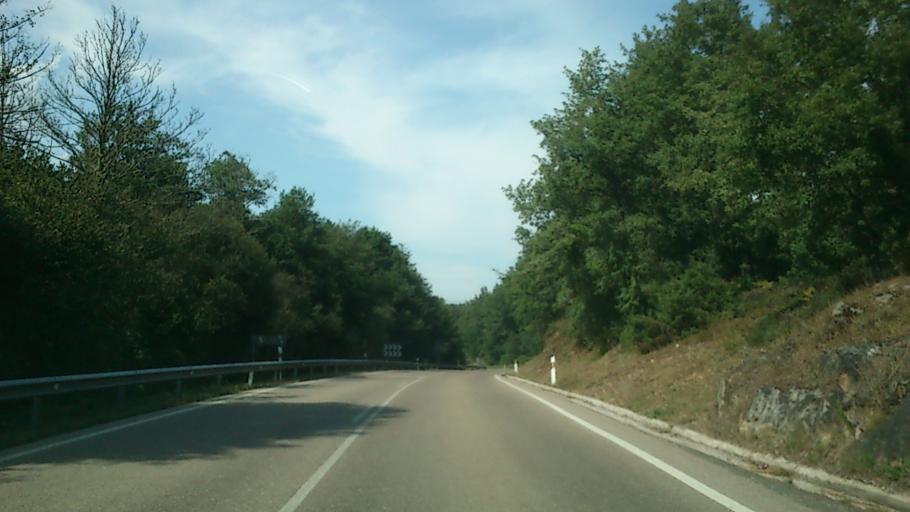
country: ES
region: Castille and Leon
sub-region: Provincia de Burgos
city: Medina de Pomar
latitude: 43.0181
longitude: -3.4835
